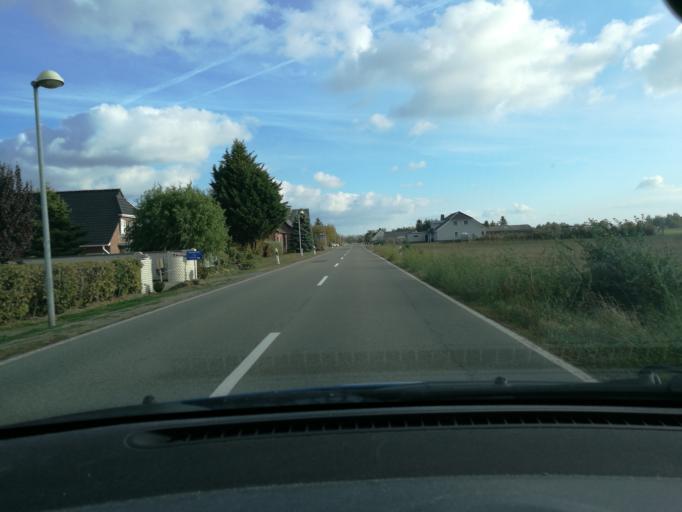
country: DE
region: Saxony-Anhalt
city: Luftkurort Arendsee
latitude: 52.8776
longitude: 11.4599
